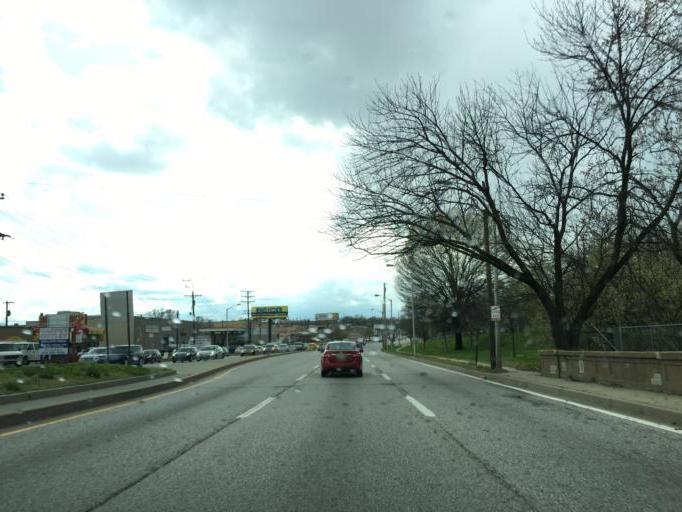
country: US
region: Maryland
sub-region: Baltimore County
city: Rosedale
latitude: 39.3053
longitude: -76.5379
